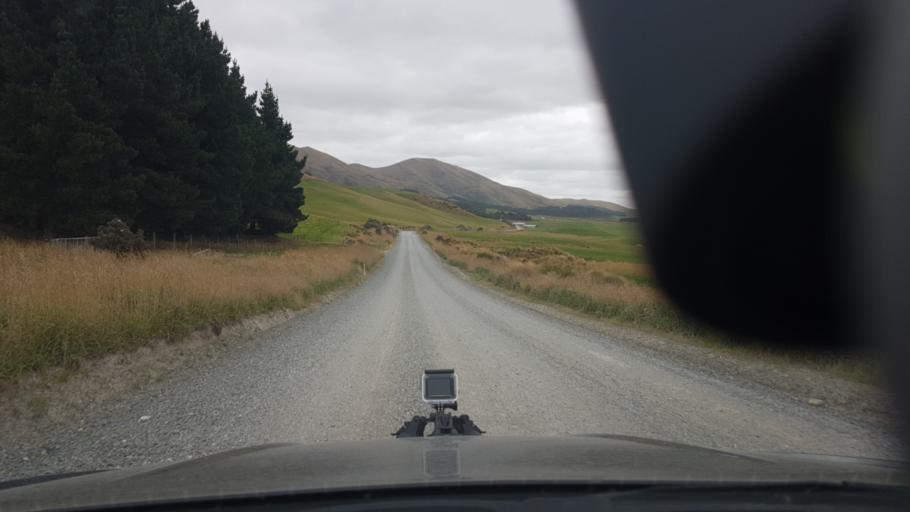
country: NZ
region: Otago
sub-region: Clutha District
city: Papatowai
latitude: -46.3265
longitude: 169.3896
